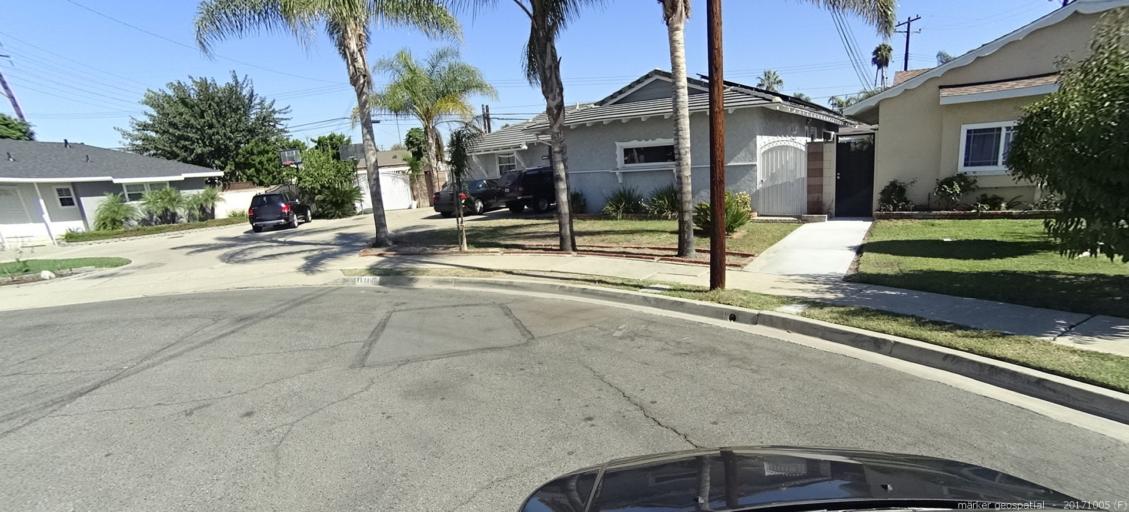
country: US
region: California
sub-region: Orange County
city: Stanton
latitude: 33.7990
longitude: -117.9793
